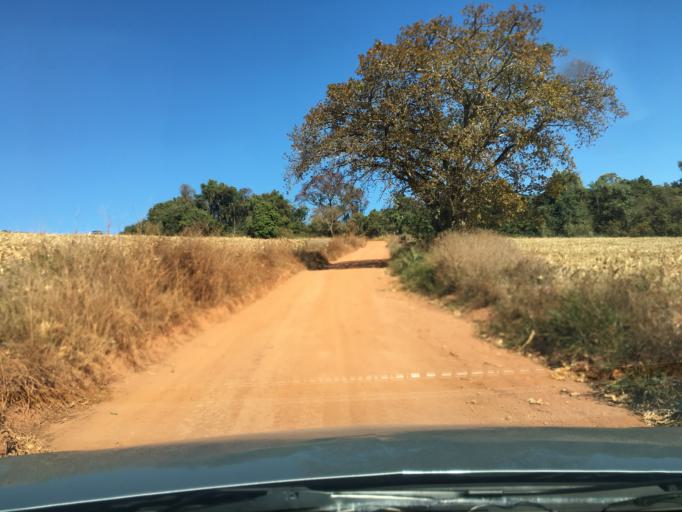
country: BR
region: Minas Gerais
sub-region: Campestre
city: Campestre
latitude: -21.5834
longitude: -46.2053
